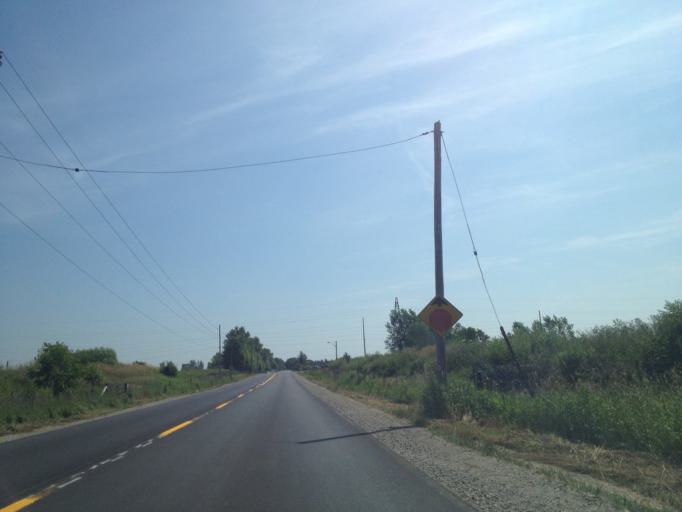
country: CA
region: Ontario
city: London
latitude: 43.0624
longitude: -81.2072
